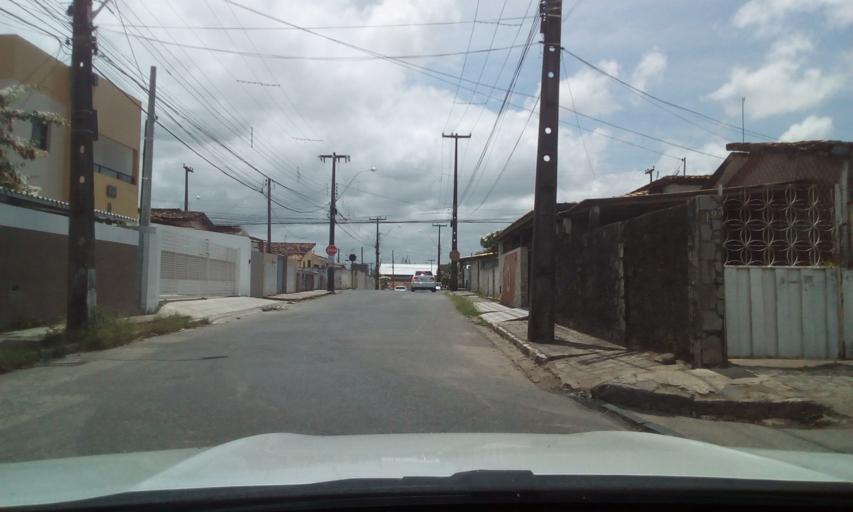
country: BR
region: Paraiba
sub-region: Bayeux
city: Bayeux
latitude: -7.1773
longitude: -34.8944
